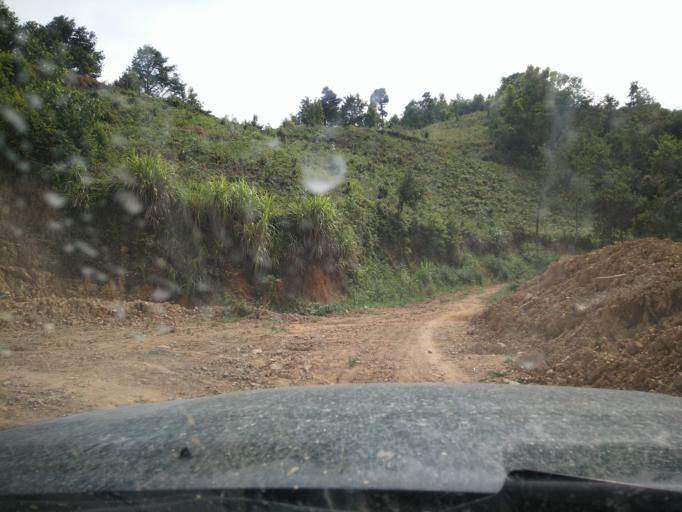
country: CN
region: Guangxi Zhuangzu Zizhiqu
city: Leli
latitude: 24.7725
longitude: 105.9076
